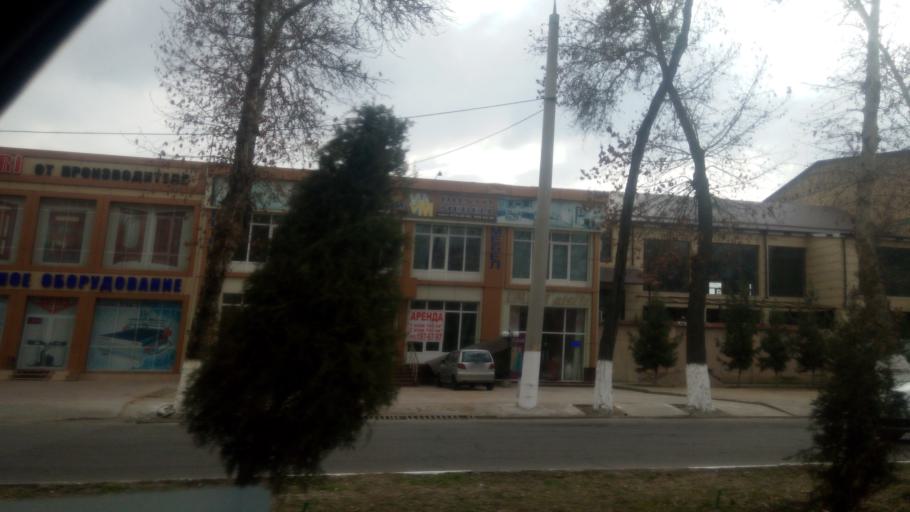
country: UZ
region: Toshkent Shahri
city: Tashkent
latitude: 41.3493
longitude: 69.2362
